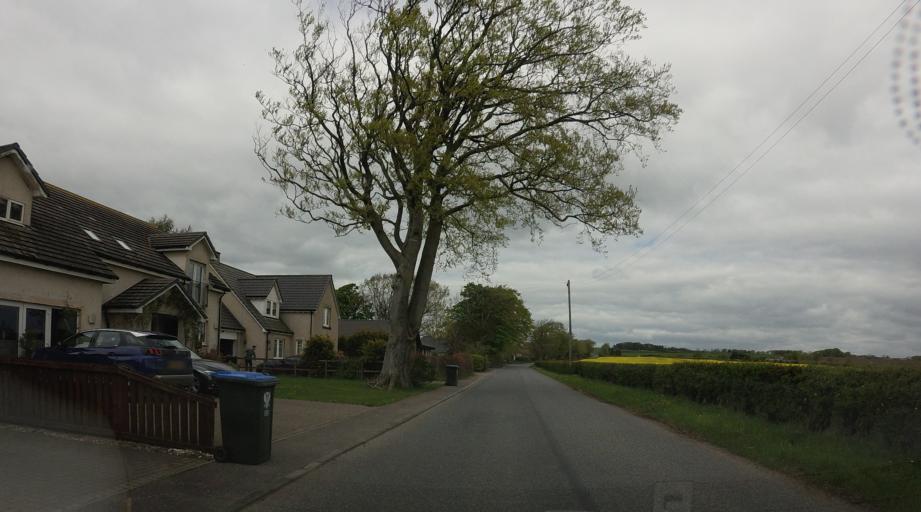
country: GB
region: Scotland
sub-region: Perth and Kinross
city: Milnathort
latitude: 56.2408
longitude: -3.3705
